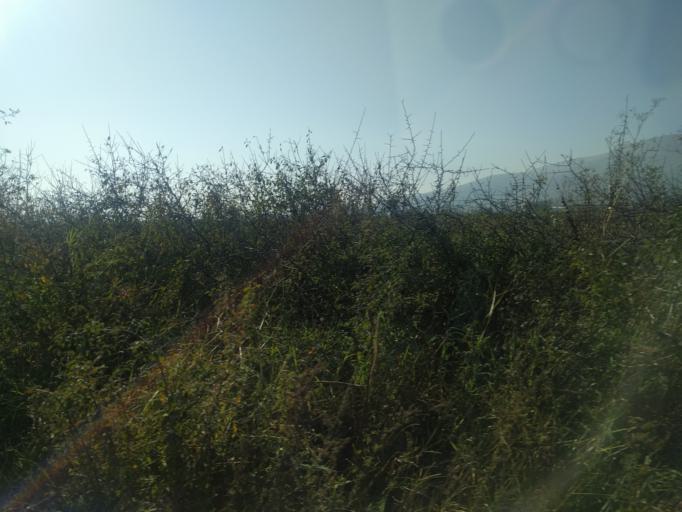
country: XK
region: Pristina
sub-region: Komuna e Gracanices
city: Glanica
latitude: 42.5871
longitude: 21.0179
